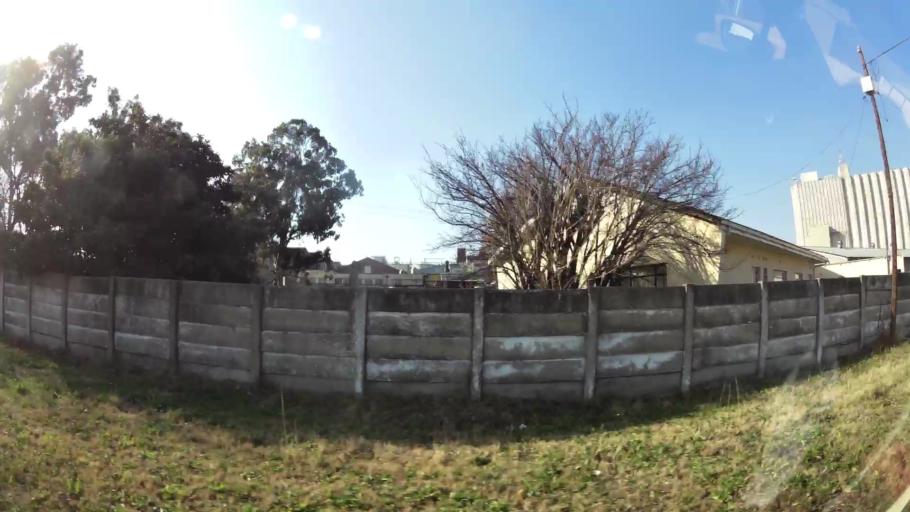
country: ZA
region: Gauteng
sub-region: West Rand District Municipality
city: Randfontein
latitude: -26.1663
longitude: 27.7102
